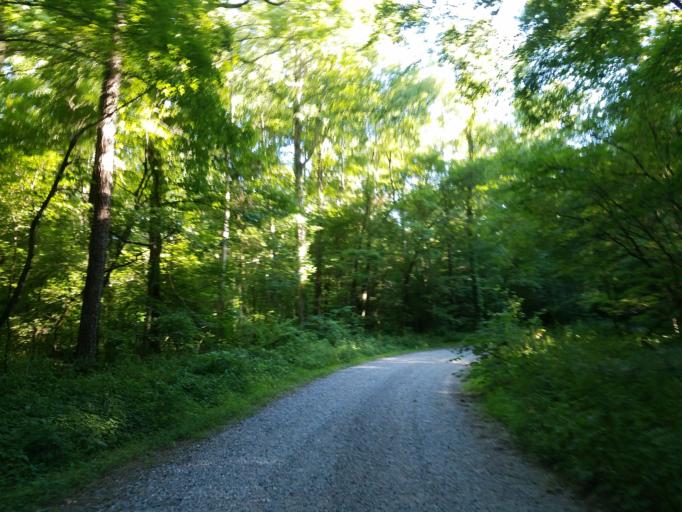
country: US
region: Georgia
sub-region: Gordon County
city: Calhoun
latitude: 34.6142
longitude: -85.0464
